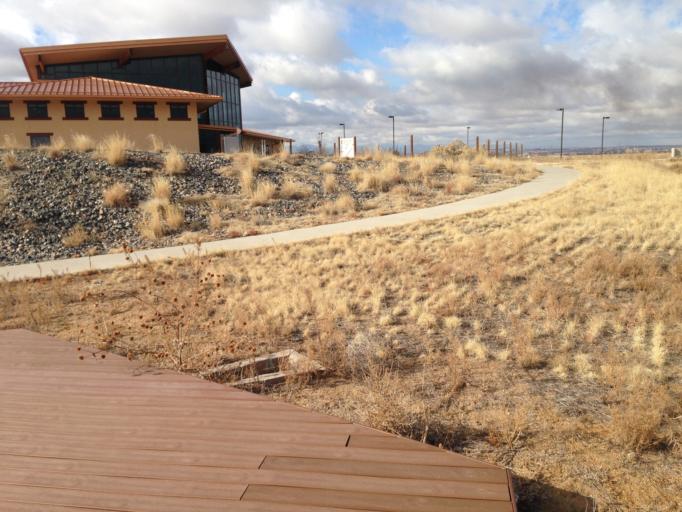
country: US
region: Colorado
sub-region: Adams County
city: Derby
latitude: 39.8151
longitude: -104.8796
